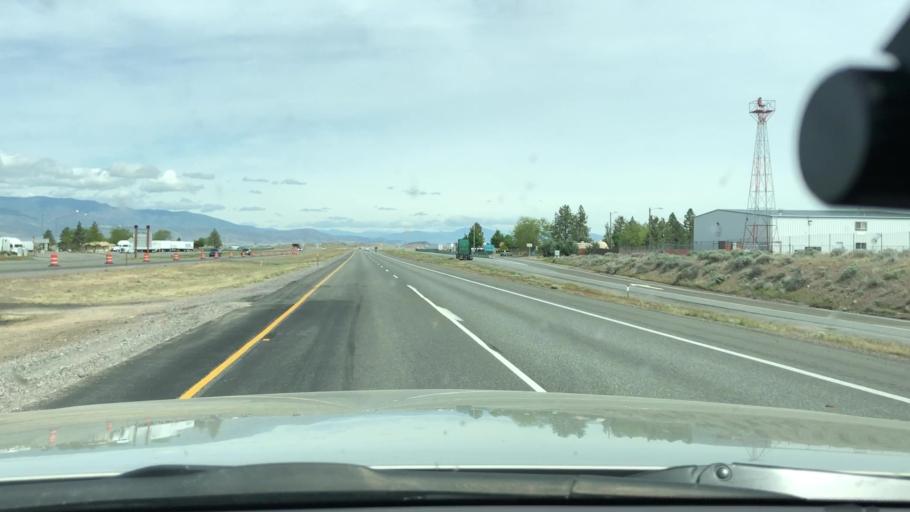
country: US
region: California
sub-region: Siskiyou County
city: Weed
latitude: 41.4747
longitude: -122.4539
